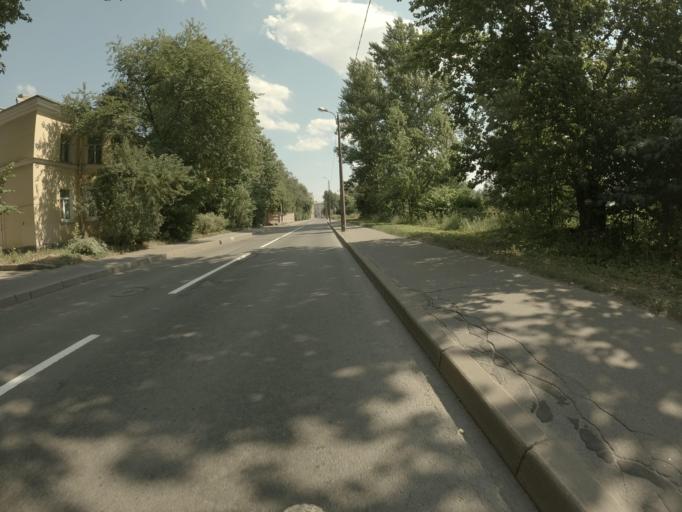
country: RU
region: St.-Petersburg
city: Avtovo
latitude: 59.8885
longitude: 30.2632
